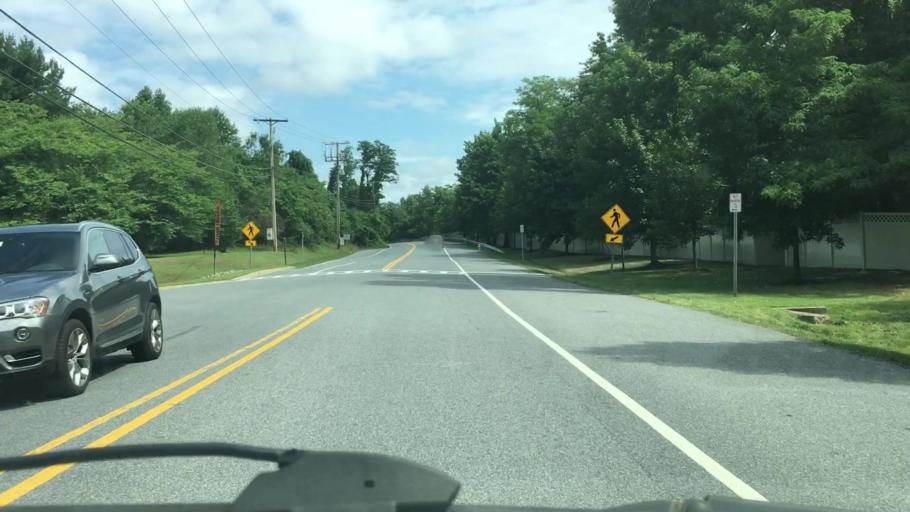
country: US
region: Maryland
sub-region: Anne Arundel County
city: Pasadena
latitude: 39.0988
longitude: -76.5775
